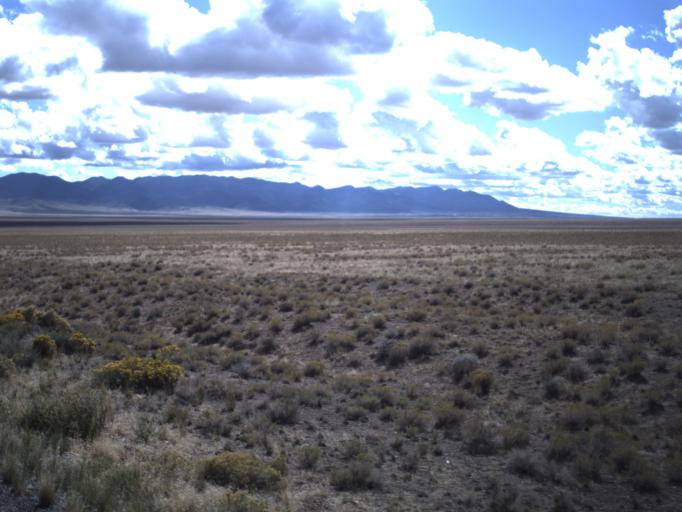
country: US
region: Utah
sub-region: Beaver County
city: Milford
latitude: 38.5606
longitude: -113.7585
